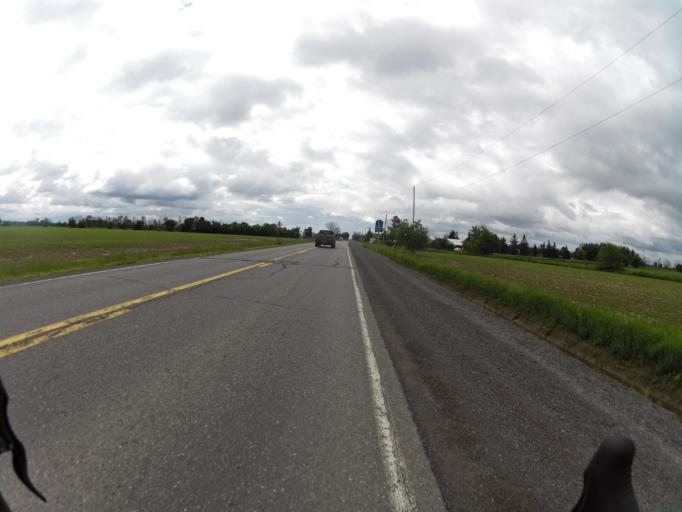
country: CA
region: Ontario
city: Bells Corners
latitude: 45.2674
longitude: -75.8566
